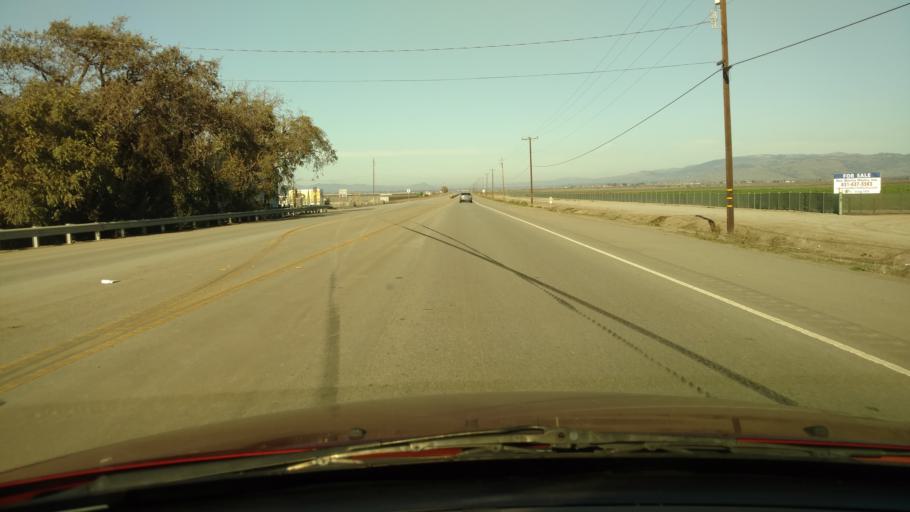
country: US
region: California
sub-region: San Benito County
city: Hollister
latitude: 36.9084
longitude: -121.4398
